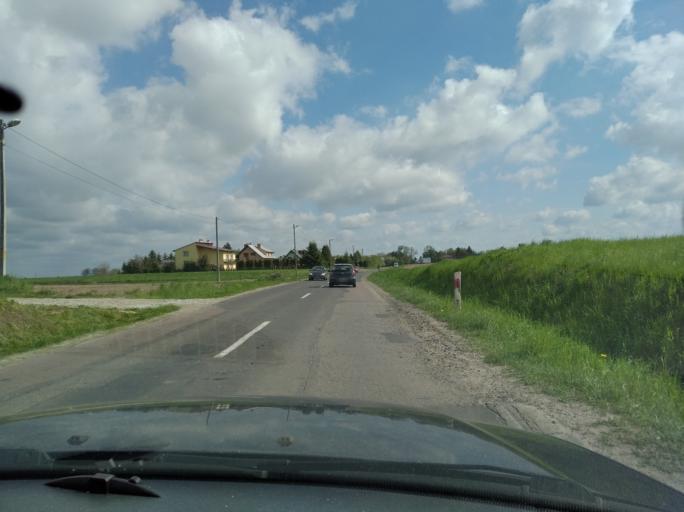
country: PL
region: Subcarpathian Voivodeship
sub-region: Powiat przeworski
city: Urzejowice
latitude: 50.0239
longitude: 22.4640
